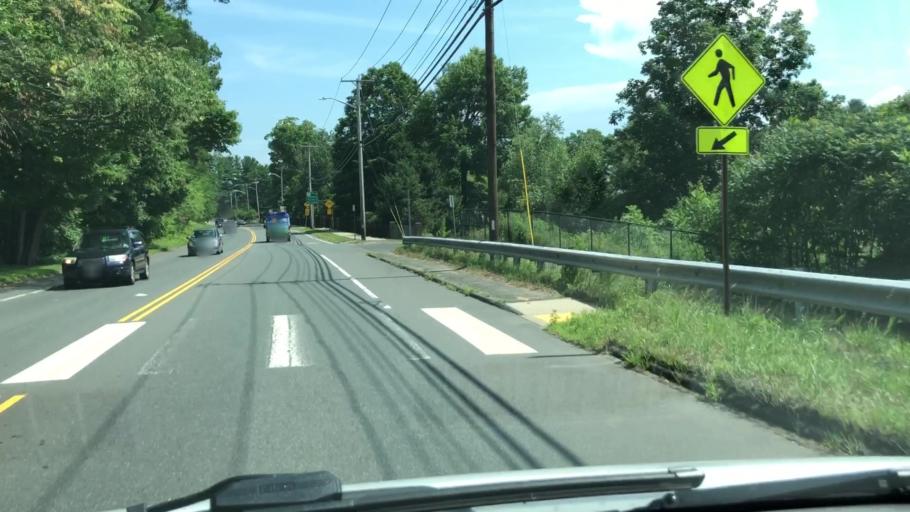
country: US
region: Massachusetts
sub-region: Hampshire County
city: Northampton
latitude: 42.3454
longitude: -72.6833
